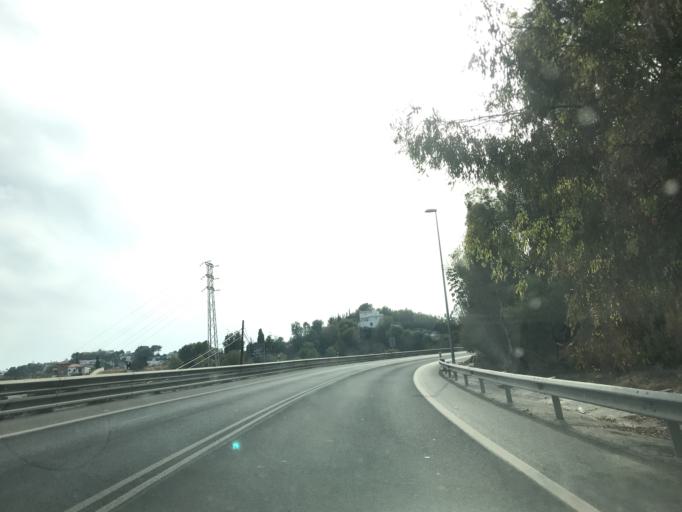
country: ES
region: Andalusia
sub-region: Provincia de Granada
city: Almunecar
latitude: 36.7447
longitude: -3.6672
